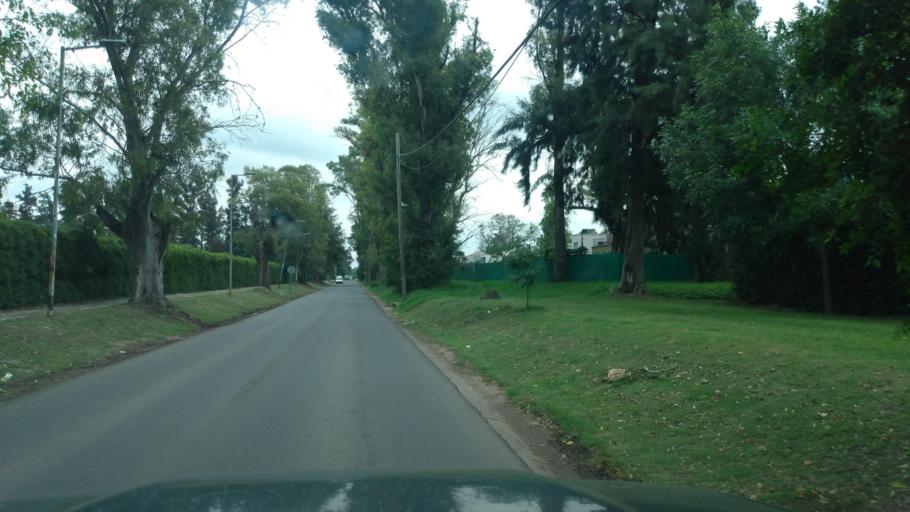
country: AR
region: Buenos Aires
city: Hurlingham
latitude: -34.5746
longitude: -58.7044
